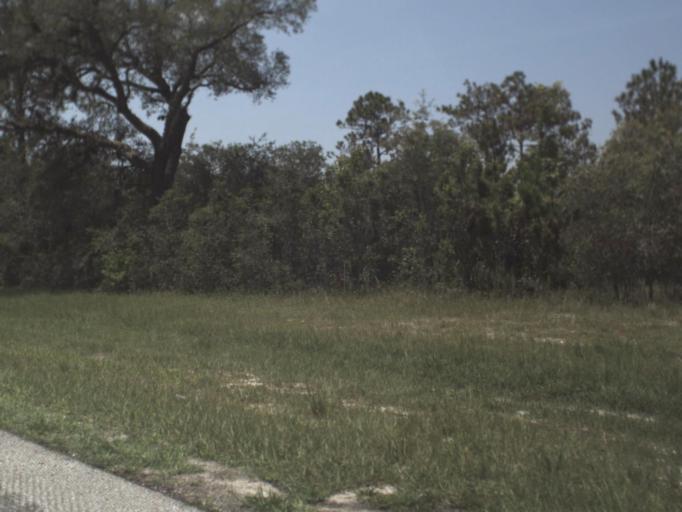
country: US
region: Florida
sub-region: Hernando County
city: North Weeki Wachee
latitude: 28.6329
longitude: -82.5521
